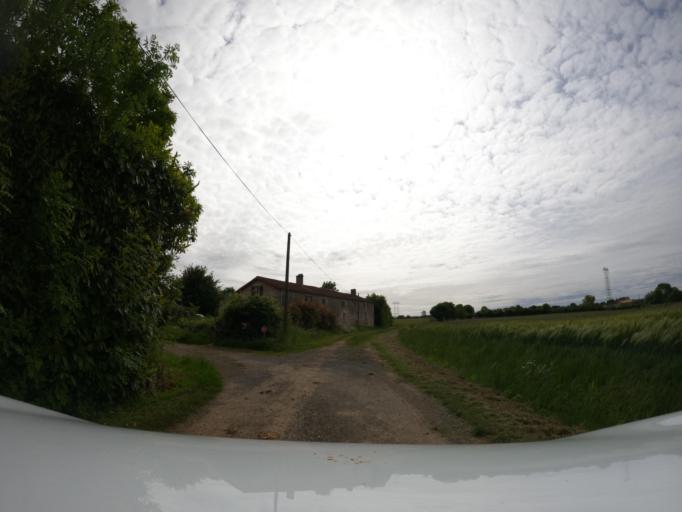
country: FR
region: Pays de la Loire
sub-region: Departement de la Vendee
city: Saint-Hilaire-des-Loges
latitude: 46.4919
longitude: -0.6654
